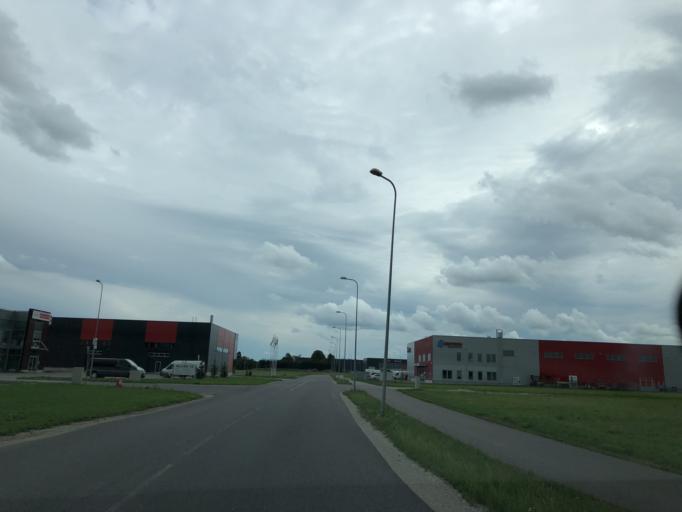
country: EE
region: Harju
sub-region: Rae vald
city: Jueri
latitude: 59.3915
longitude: 24.8226
